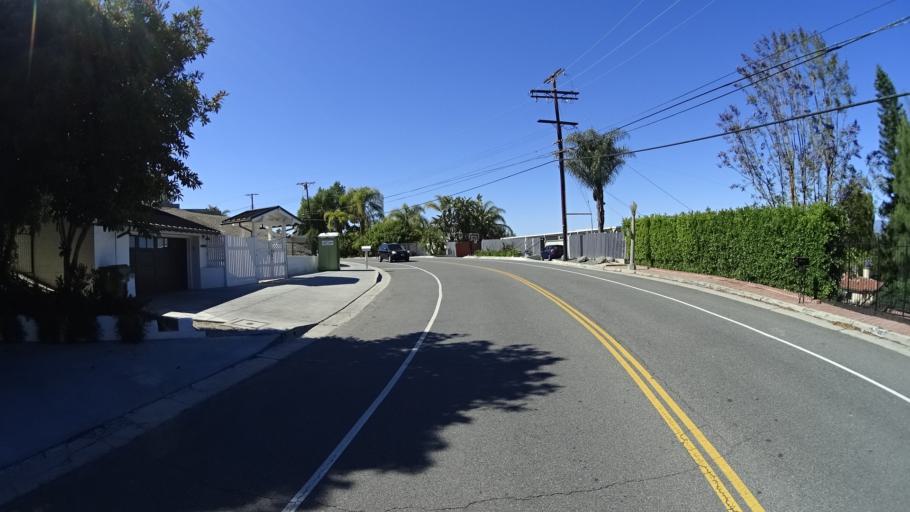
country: US
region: California
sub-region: Los Angeles County
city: Sherman Oaks
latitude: 34.1466
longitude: -118.4567
